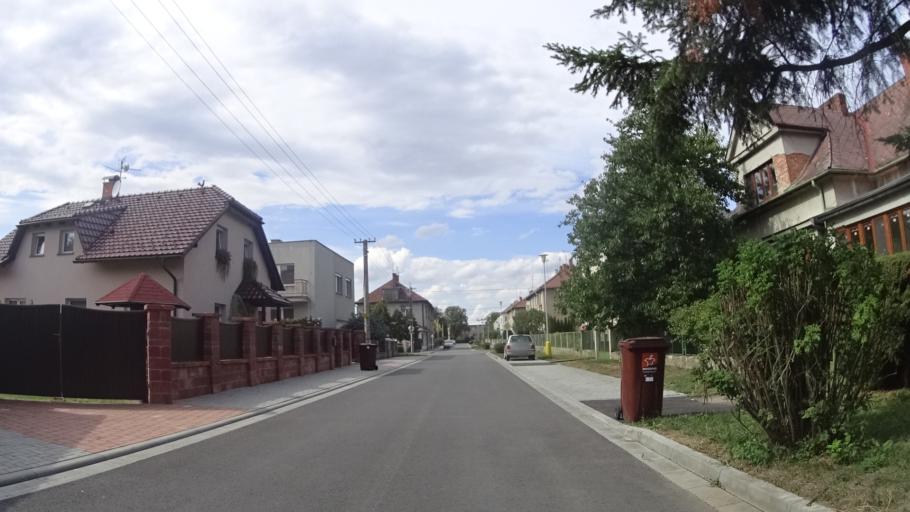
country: CZ
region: Olomoucky
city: Litovel
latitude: 49.6997
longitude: 17.0865
